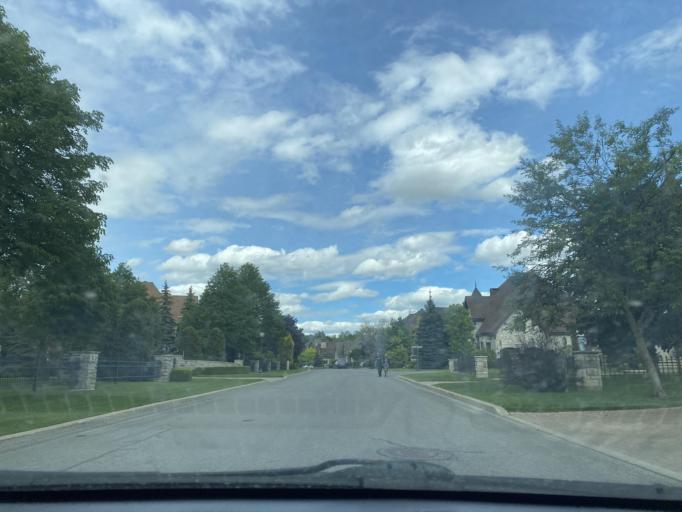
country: CA
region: Quebec
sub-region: Monteregie
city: Carignan
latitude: 45.4728
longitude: -73.2938
